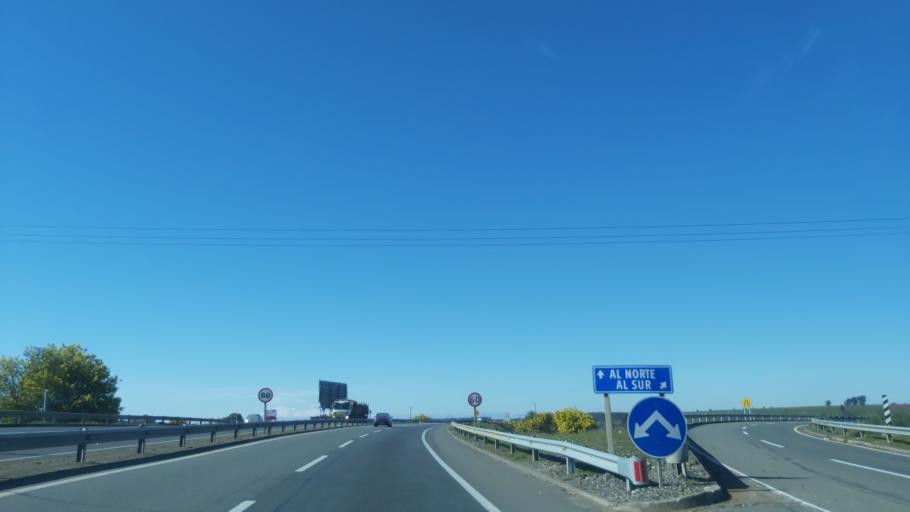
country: CL
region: Biobio
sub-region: Provincia de Nuble
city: Bulnes
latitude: -36.6542
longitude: -72.2335
